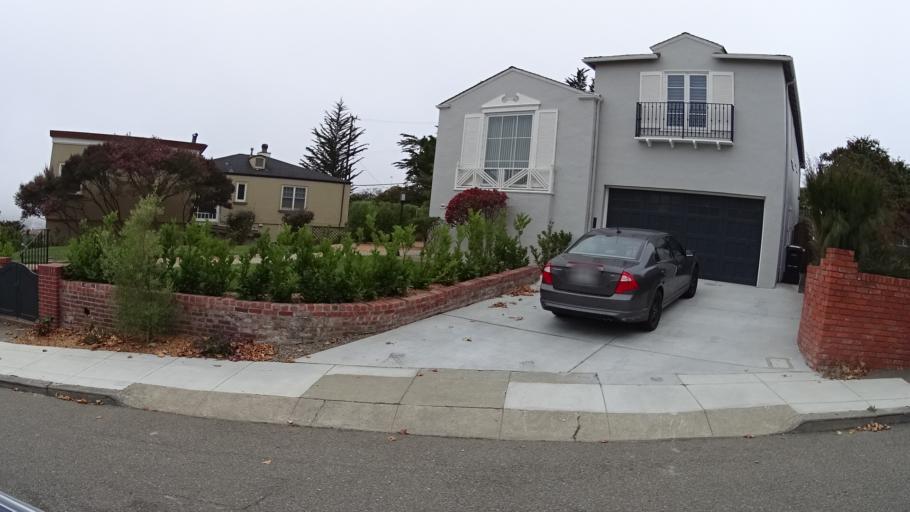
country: US
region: California
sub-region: San Mateo County
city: Daly City
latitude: 37.7315
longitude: -122.4614
